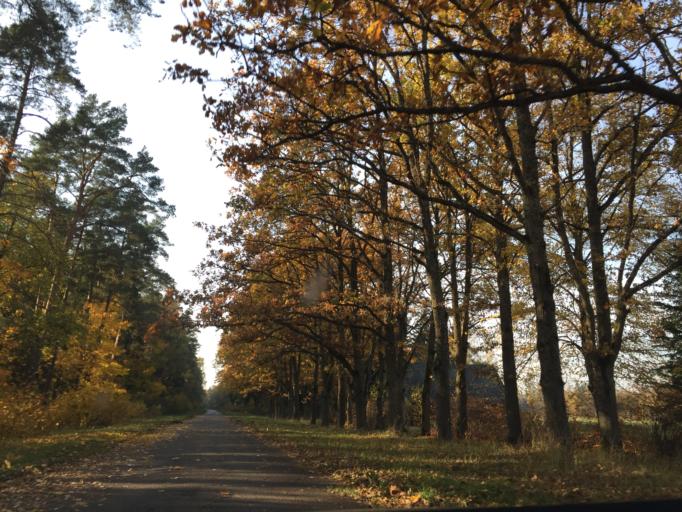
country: LV
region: Skrunda
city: Skrunda
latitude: 56.6784
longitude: 22.1542
